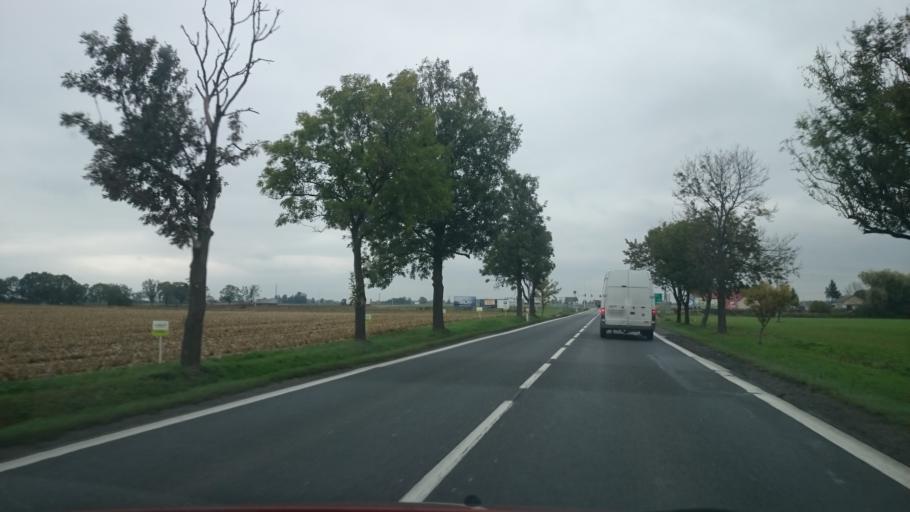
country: PL
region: Lower Silesian Voivodeship
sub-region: Powiat wroclawski
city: Kobierzyce
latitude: 50.9867
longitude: 16.9488
